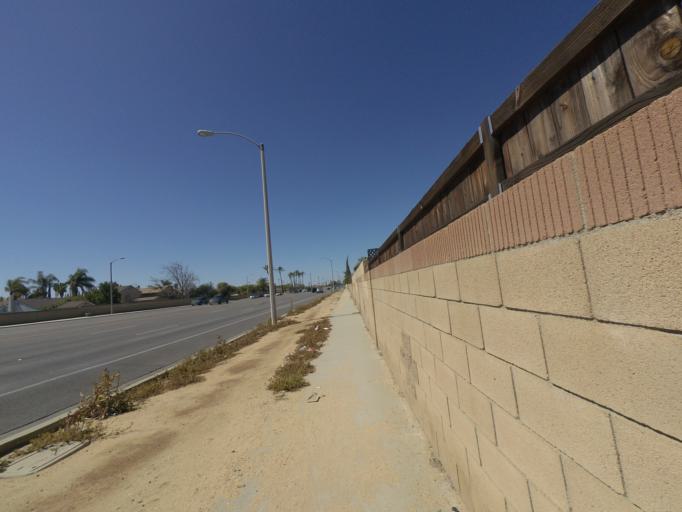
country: US
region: California
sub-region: Riverside County
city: Moreno Valley
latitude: 33.9175
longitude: -117.2398
